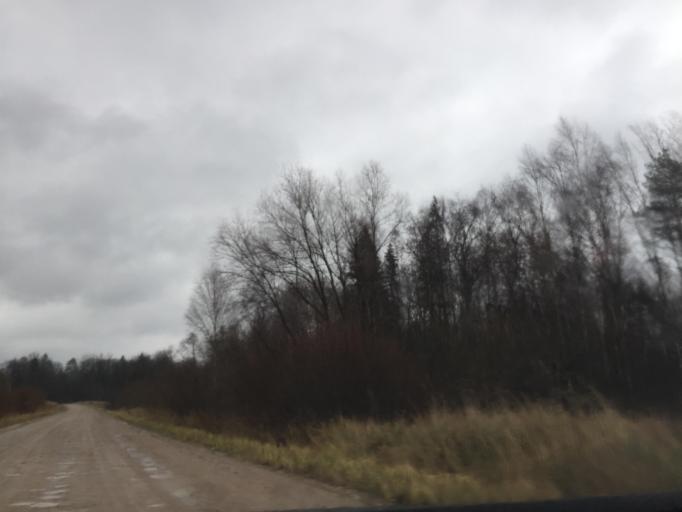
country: LV
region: Limbazu Rajons
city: Limbazi
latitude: 57.6423
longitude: 24.7746
